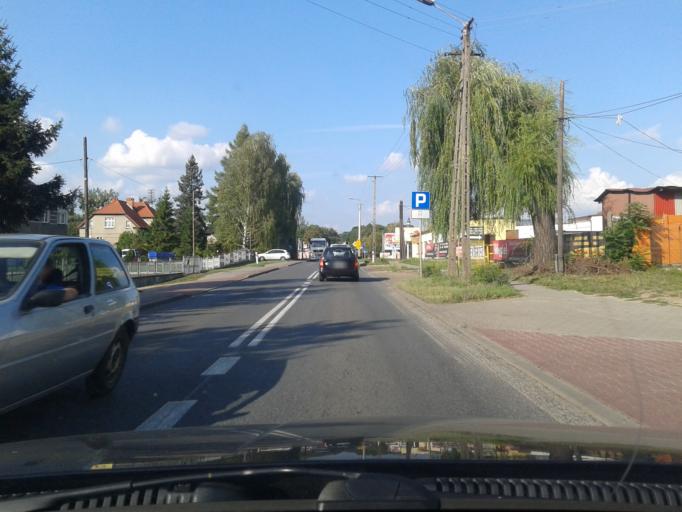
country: PL
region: Silesian Voivodeship
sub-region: Powiat wodzislawski
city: Wodzislaw Slaski
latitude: 49.9952
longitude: 18.4577
